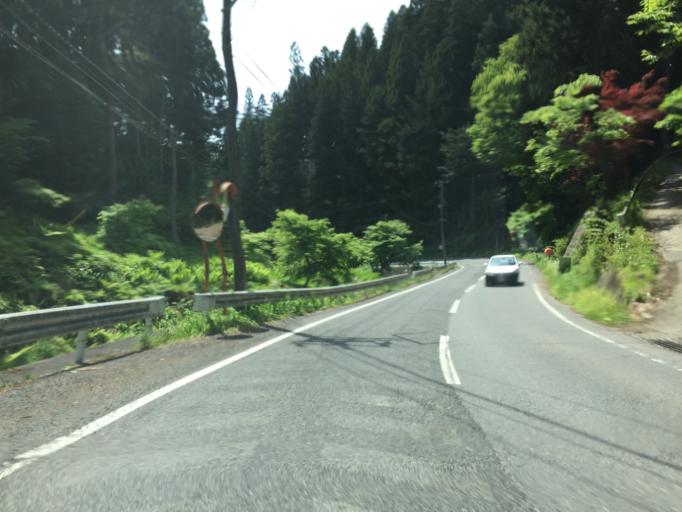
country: JP
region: Fukushima
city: Ishikawa
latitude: 37.1528
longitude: 140.4864
